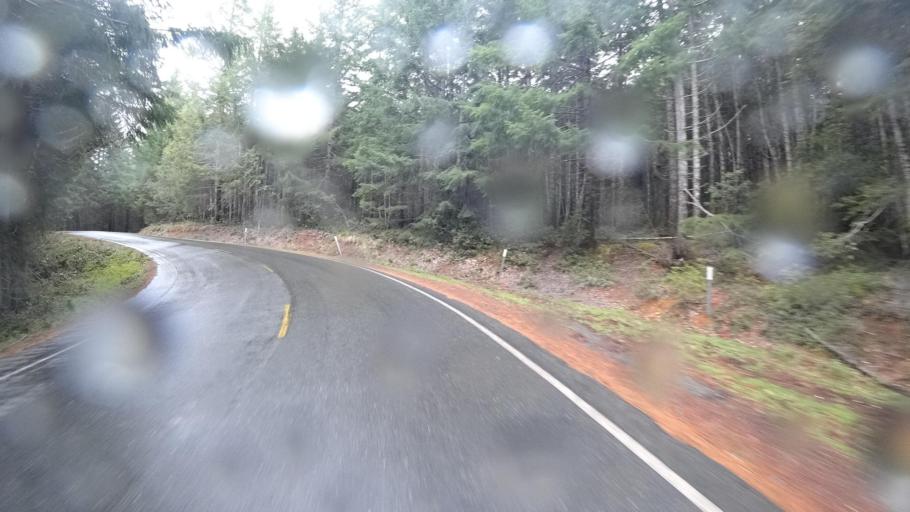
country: US
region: California
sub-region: Humboldt County
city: Willow Creek
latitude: 41.1956
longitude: -123.8087
